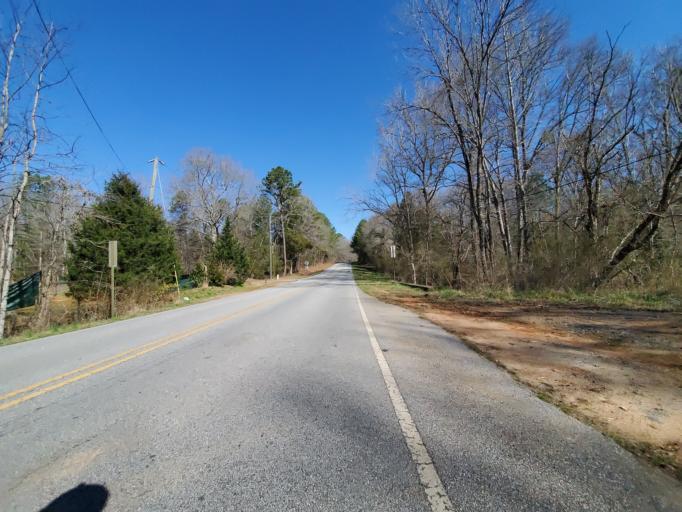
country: US
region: Georgia
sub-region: Oconee County
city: Bogart
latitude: 33.9983
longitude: -83.4955
